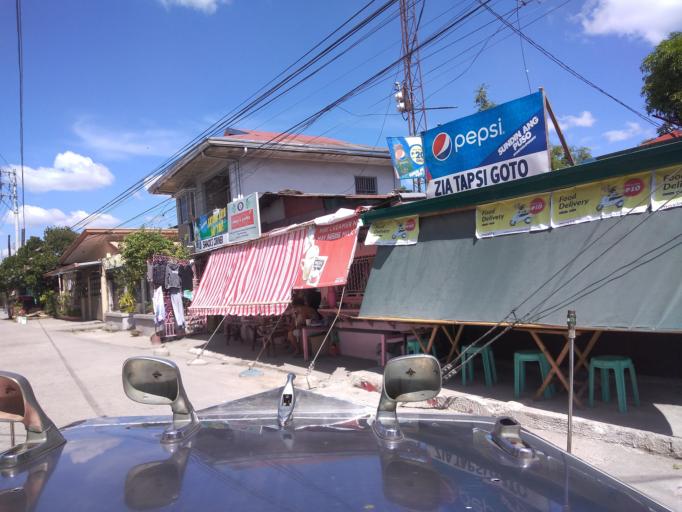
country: PH
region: Central Luzon
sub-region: Province of Pampanga
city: Calibutbut
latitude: 15.1182
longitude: 120.6019
